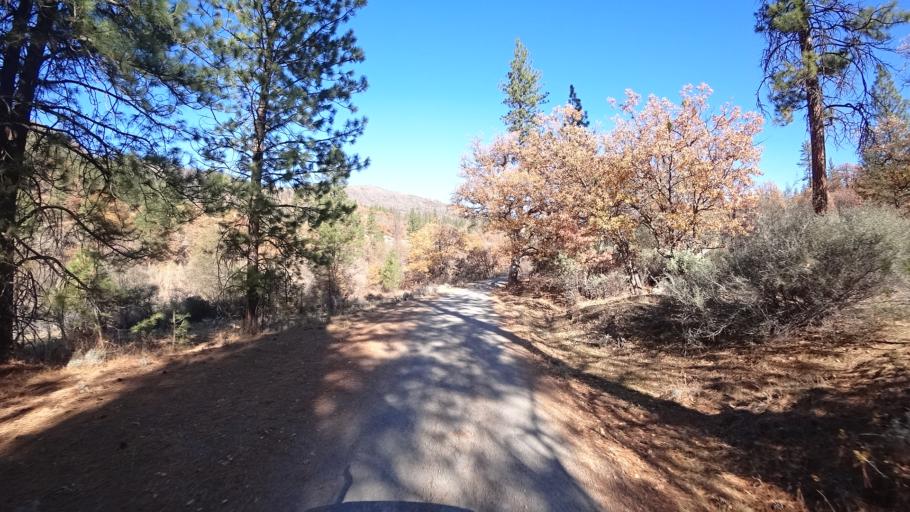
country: US
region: California
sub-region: Siskiyou County
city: Yreka
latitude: 41.8476
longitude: -122.8362
